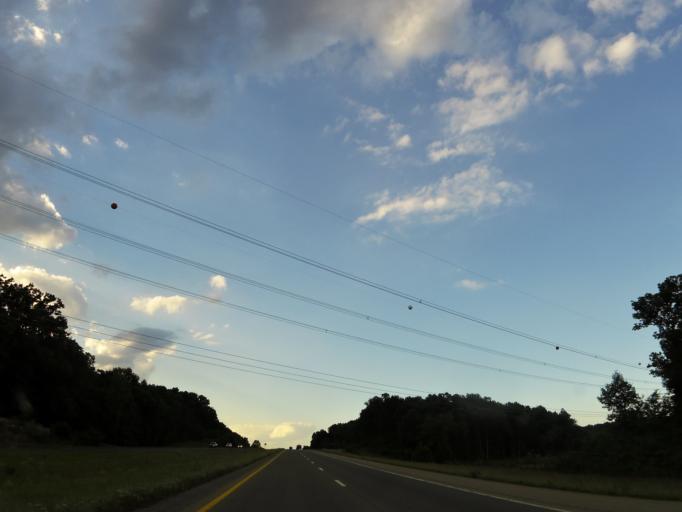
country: US
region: Tennessee
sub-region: Maury County
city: Spring Hill
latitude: 35.7087
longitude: -86.8805
